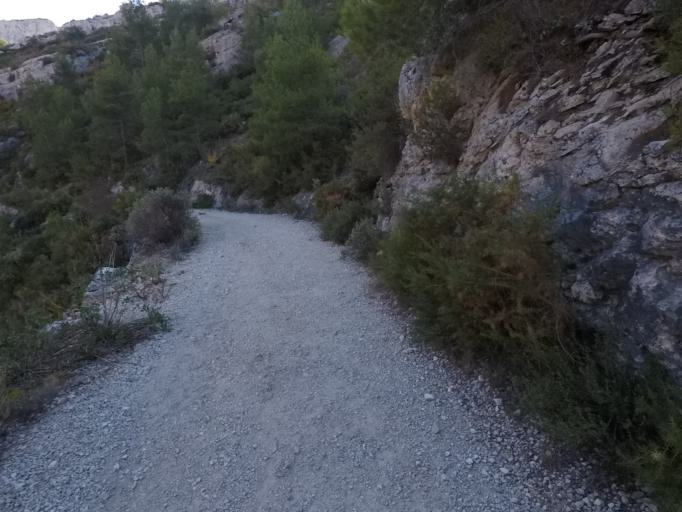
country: FR
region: Provence-Alpes-Cote d'Azur
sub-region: Departement des Bouches-du-Rhone
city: La Penne-sur-Huveaune
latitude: 43.2702
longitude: 5.4873
